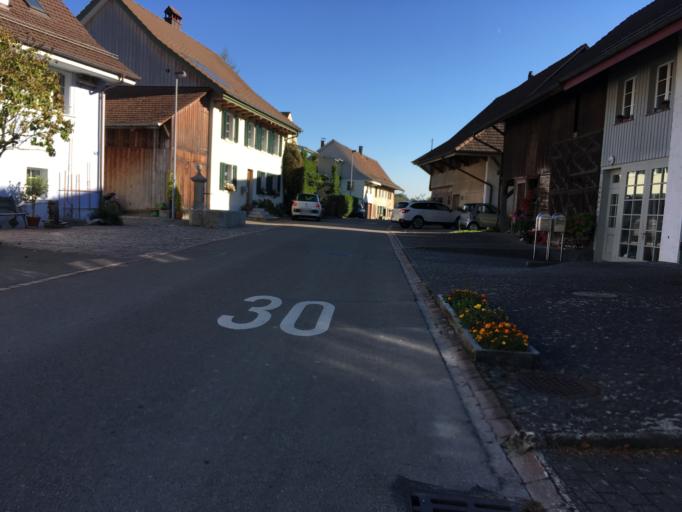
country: CH
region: Zurich
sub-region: Bezirk Buelach
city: Seglingen
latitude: 47.5645
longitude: 8.5446
